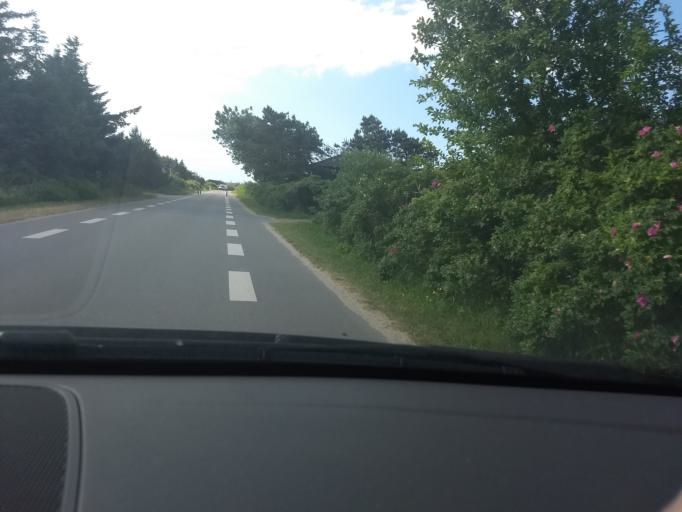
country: DE
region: Schleswig-Holstein
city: List
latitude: 55.1428
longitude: 8.4944
